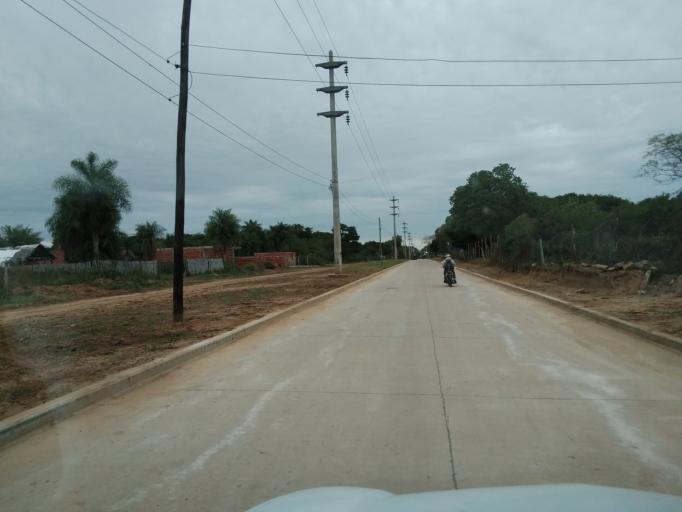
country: AR
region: Corrientes
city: Corrientes
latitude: -27.5119
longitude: -58.8218
